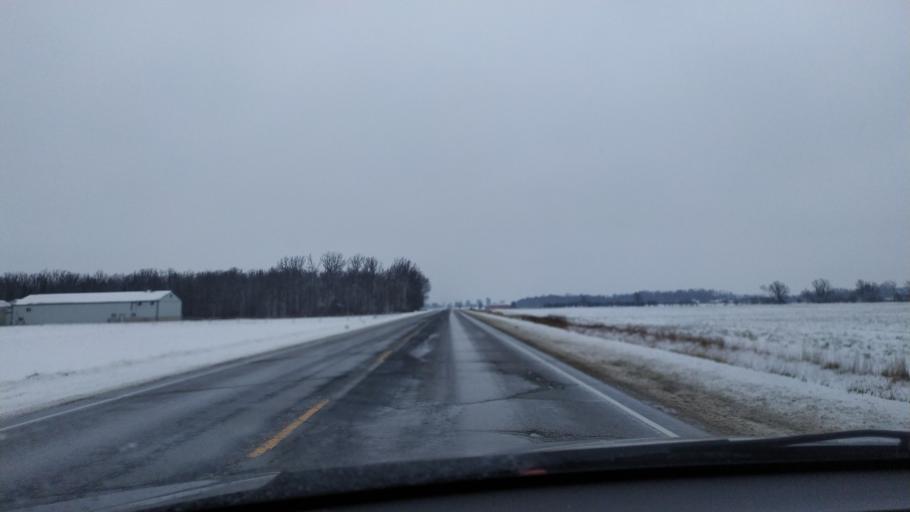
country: CA
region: Ontario
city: North Perth
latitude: 43.5857
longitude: -80.8289
